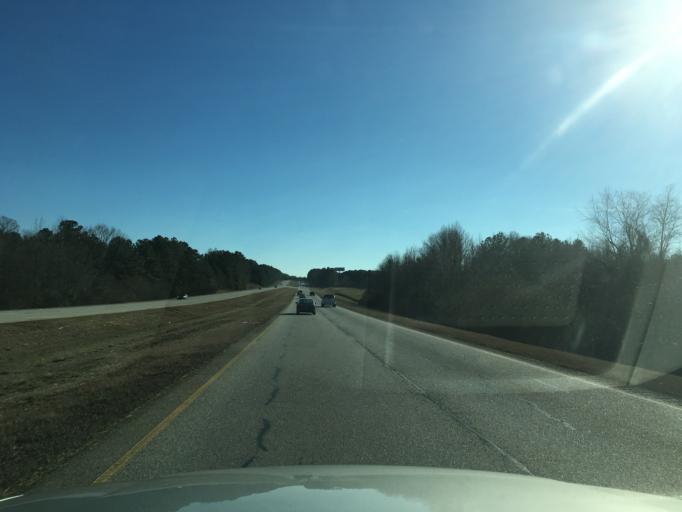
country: US
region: Georgia
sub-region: Carroll County
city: Carrollton
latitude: 33.5894
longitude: -85.0417
